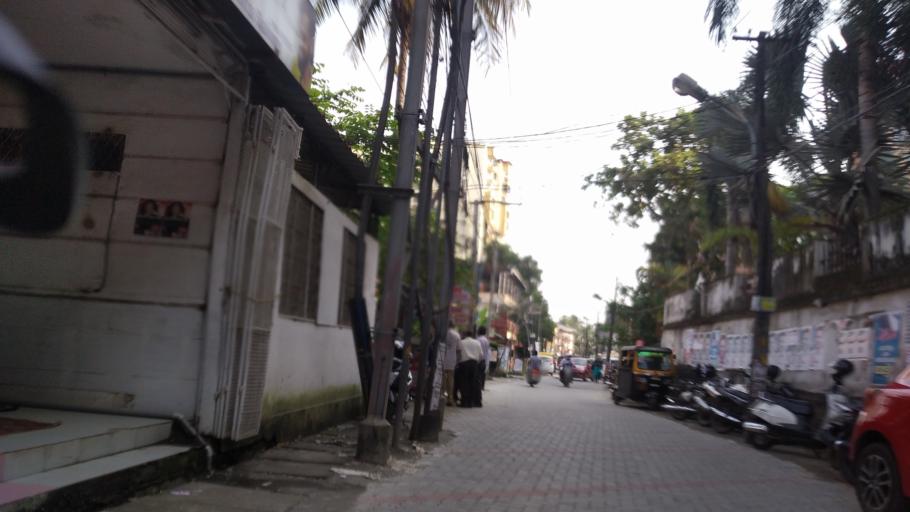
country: IN
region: Kerala
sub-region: Ernakulam
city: Cochin
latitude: 9.9880
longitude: 76.2889
